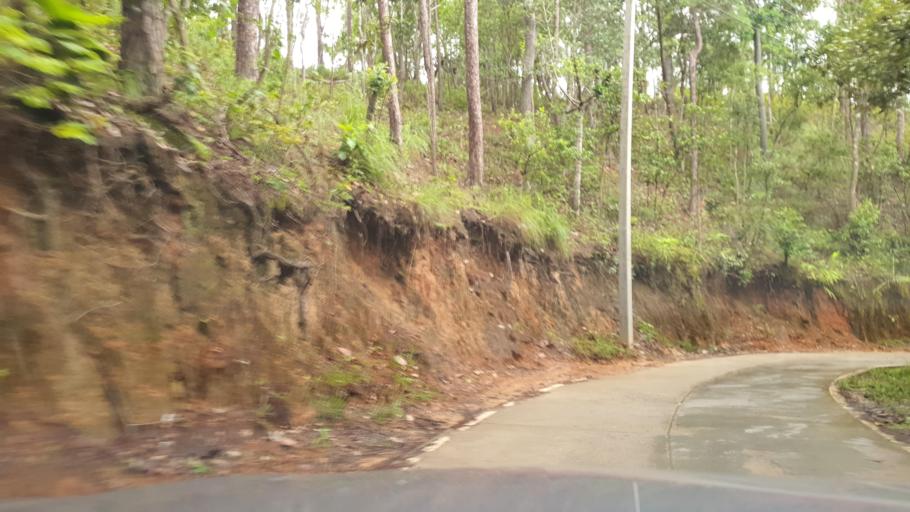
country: TH
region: Chiang Mai
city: Mae Wang
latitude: 18.6984
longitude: 98.5695
